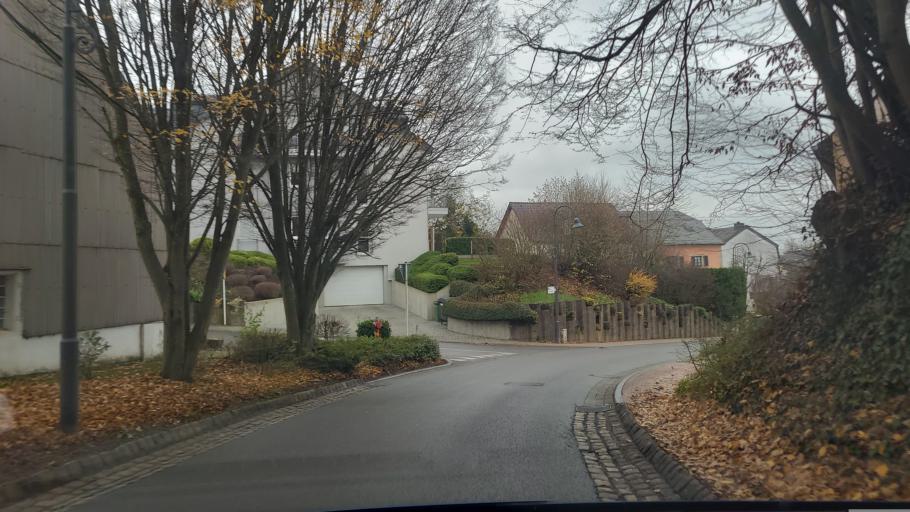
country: LU
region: Luxembourg
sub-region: Canton d'Esch-sur-Alzette
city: Mondercange
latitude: 49.5598
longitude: 5.9786
